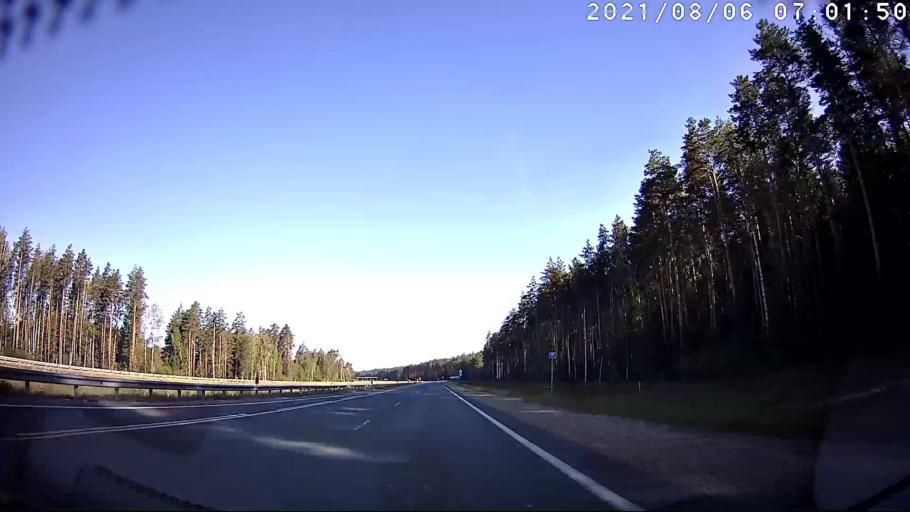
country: RU
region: Mariy-El
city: Surok
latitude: 56.5277
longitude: 48.0052
